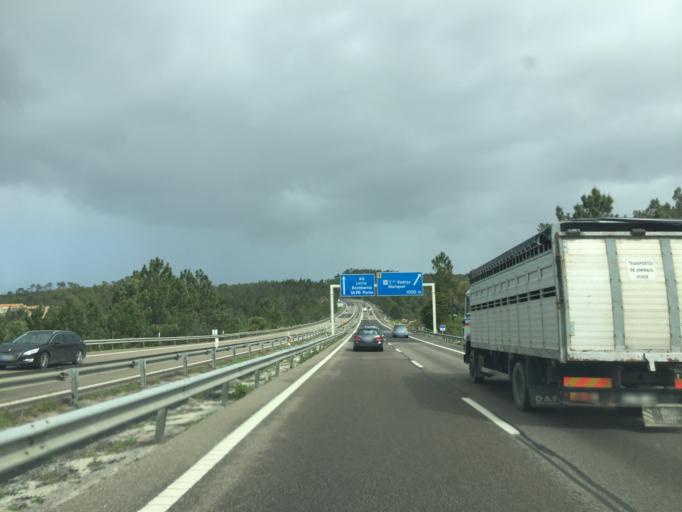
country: PT
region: Lisbon
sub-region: Torres Vedras
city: Torres Vedras
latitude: 39.0997
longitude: -9.2403
